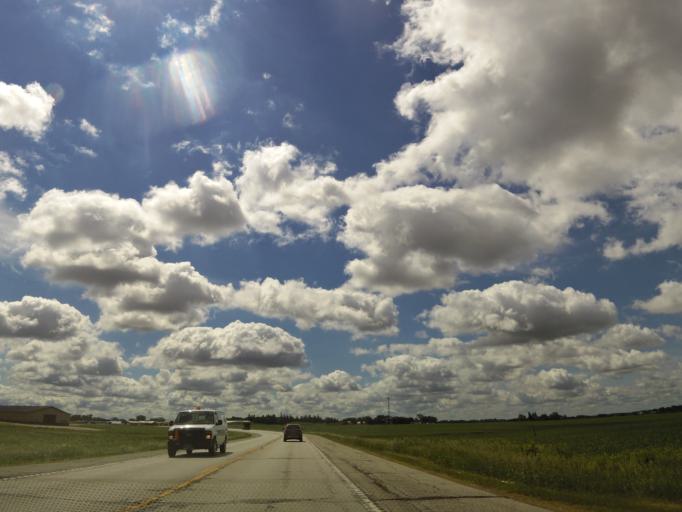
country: US
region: Minnesota
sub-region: Fillmore County
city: Spring Valley
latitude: 43.7052
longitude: -92.4139
